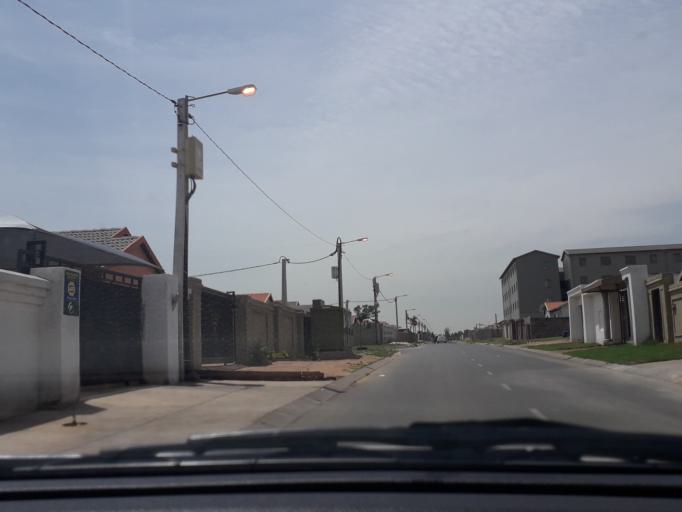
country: ZA
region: Gauteng
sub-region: City of Johannesburg Metropolitan Municipality
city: Roodepoort
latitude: -26.2042
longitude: 27.9110
